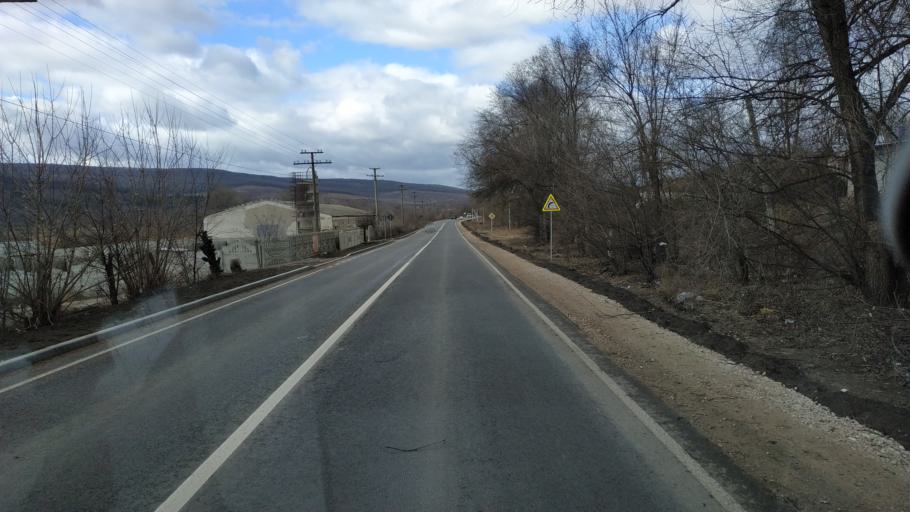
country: MD
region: Stinga Nistrului
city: Bucovat
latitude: 47.1898
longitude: 28.4480
